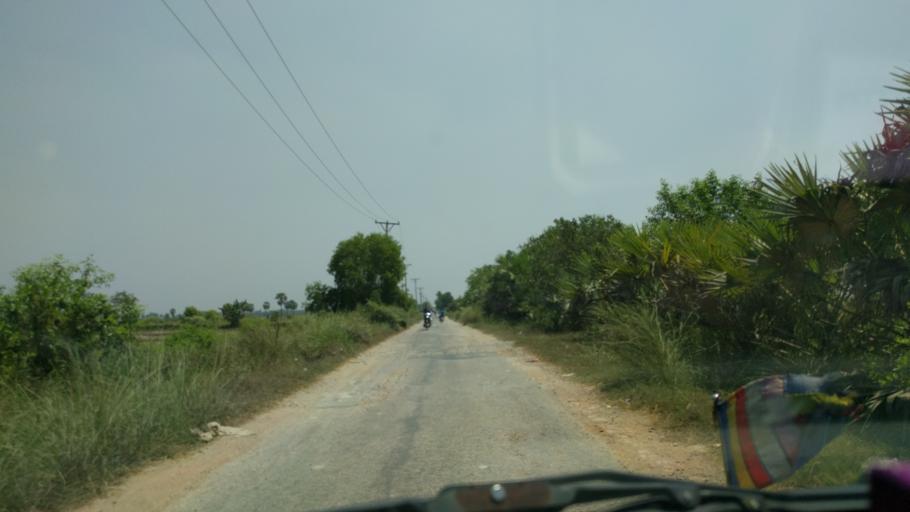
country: MM
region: Mon
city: Martaban
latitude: 16.5859
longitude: 97.6702
